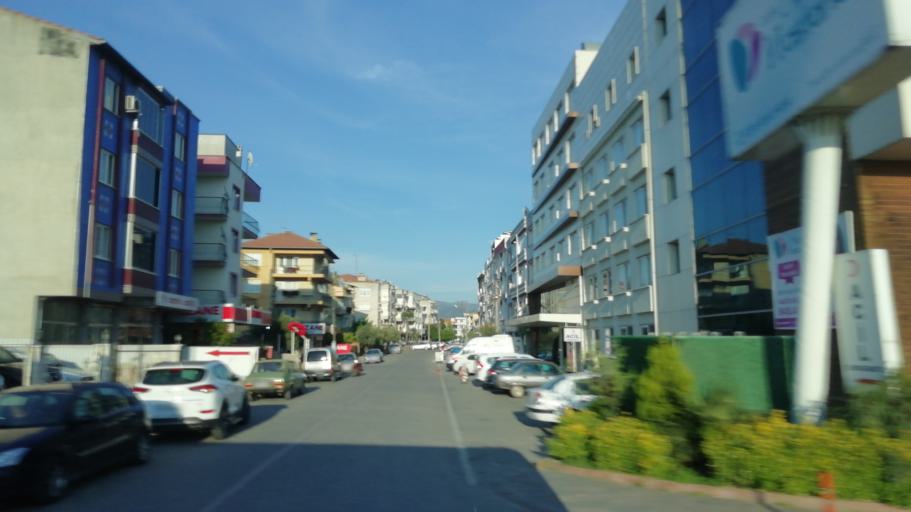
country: TR
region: Manisa
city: Akhisar
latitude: 38.9287
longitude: 27.8344
